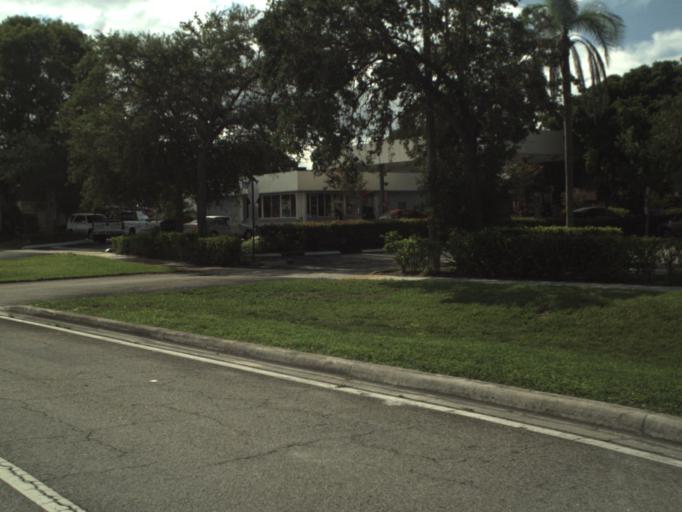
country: US
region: Florida
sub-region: Broward County
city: Plantation
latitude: 26.1676
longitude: -80.2631
